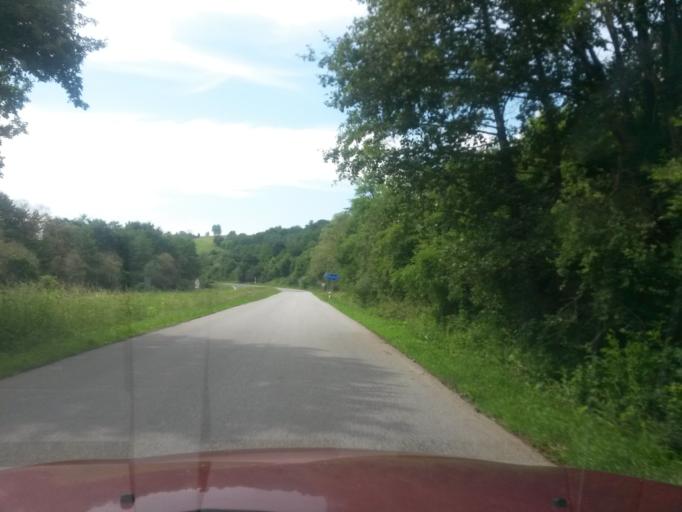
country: SK
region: Presovsky
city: Snina
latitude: 48.9872
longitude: 22.2579
